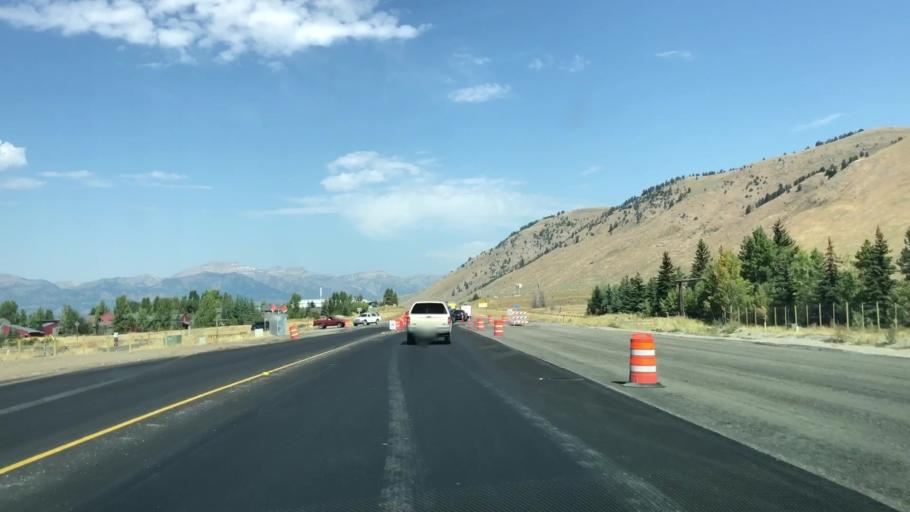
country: US
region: Wyoming
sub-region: Teton County
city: South Park
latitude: 43.4136
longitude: -110.7726
